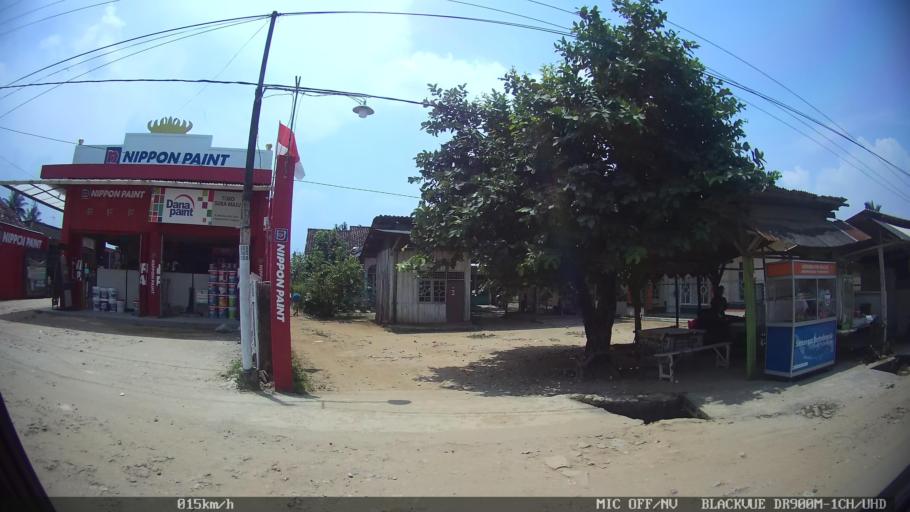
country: ID
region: Lampung
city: Natar
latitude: -5.3163
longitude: 105.2010
